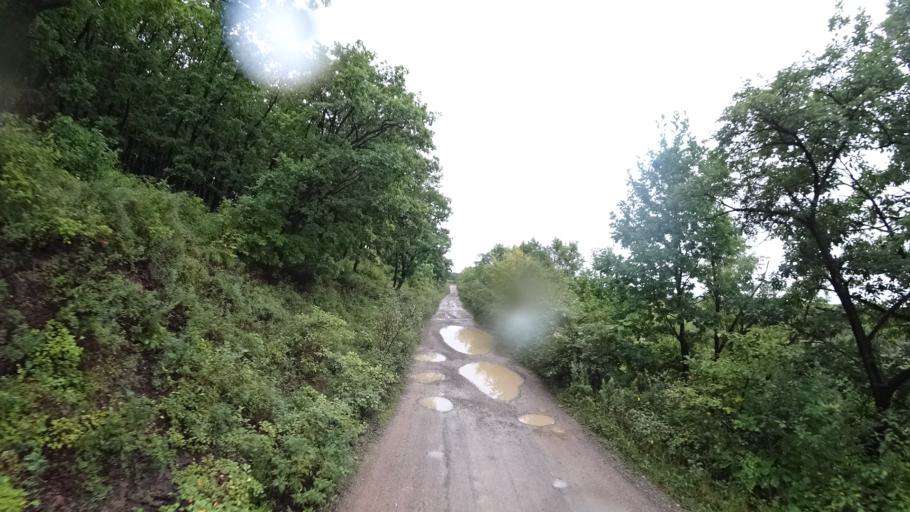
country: RU
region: Primorskiy
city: Monastyrishche
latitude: 44.2606
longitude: 132.4071
